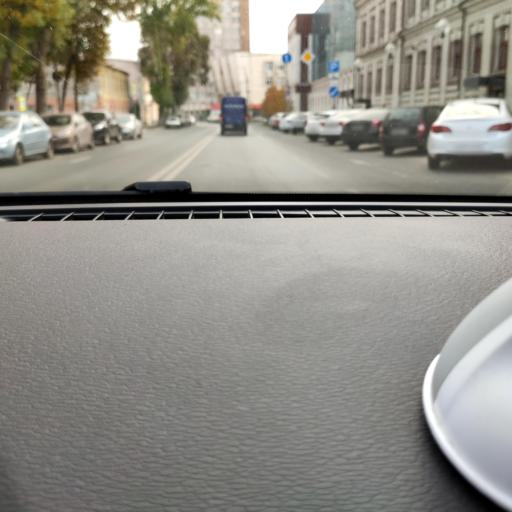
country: RU
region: Samara
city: Samara
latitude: 53.1872
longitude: 50.1151
